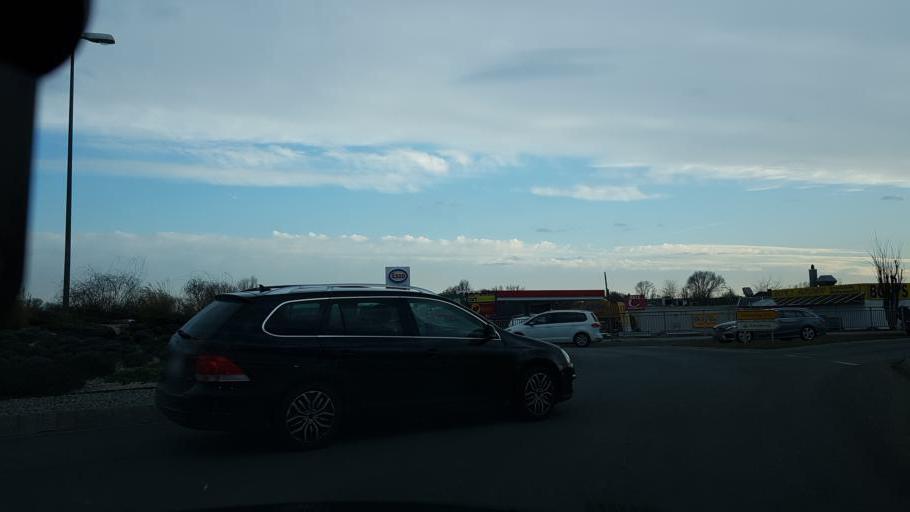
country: DE
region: Bavaria
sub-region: Upper Bavaria
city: Emmering
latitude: 48.1991
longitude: 11.3015
